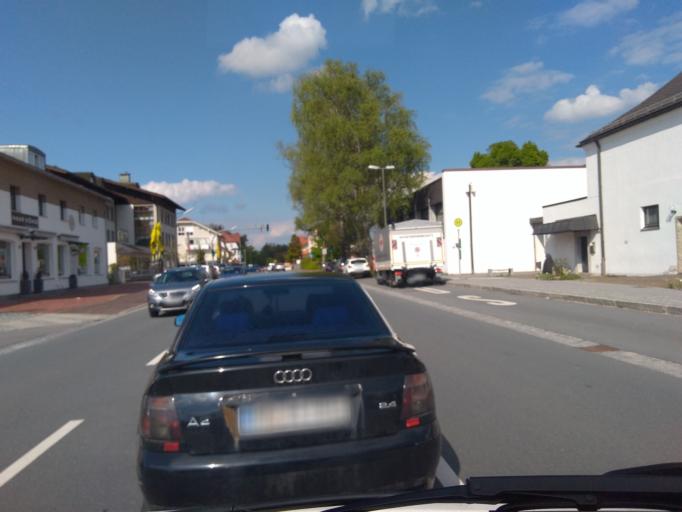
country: DE
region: Bavaria
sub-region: Upper Bavaria
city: Raubling
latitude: 47.7910
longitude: 12.1146
